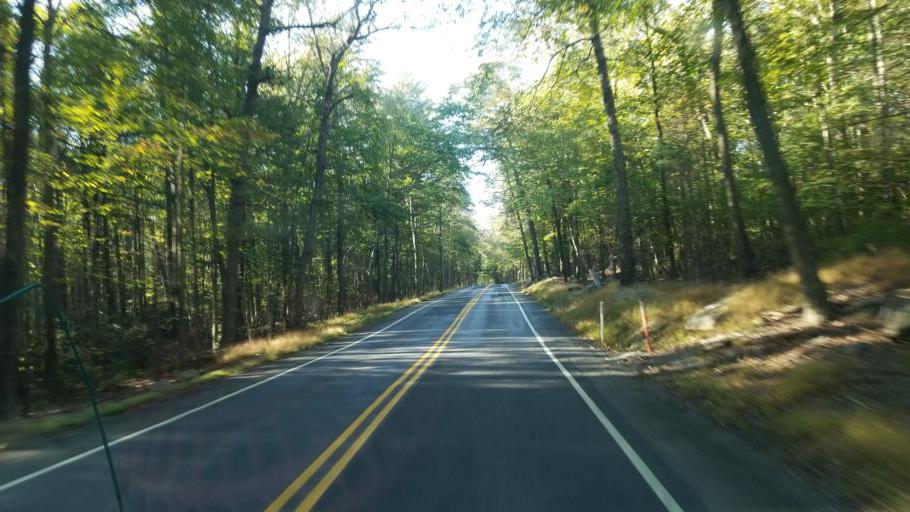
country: US
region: Pennsylvania
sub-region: Franklin County
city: Mont Alto
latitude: 39.8613
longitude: -77.5016
